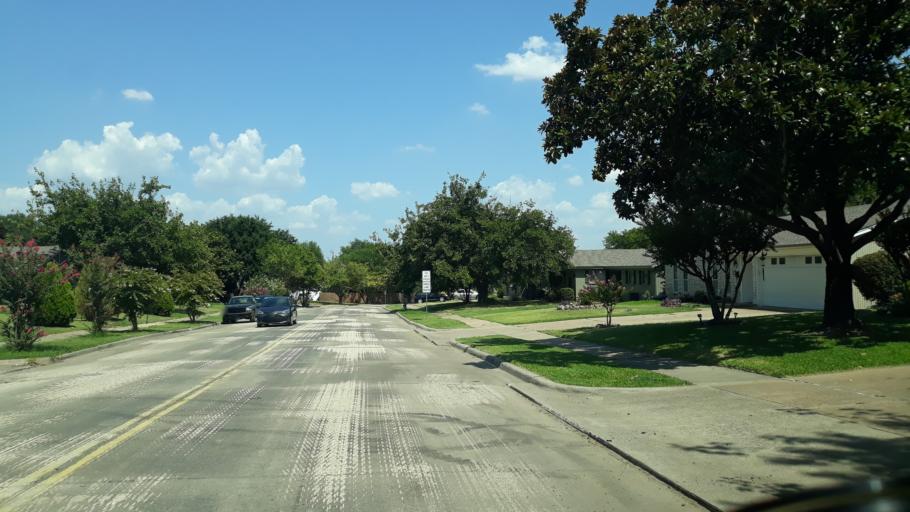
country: US
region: Texas
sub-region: Dallas County
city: Irving
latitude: 32.8514
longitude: -97.0073
